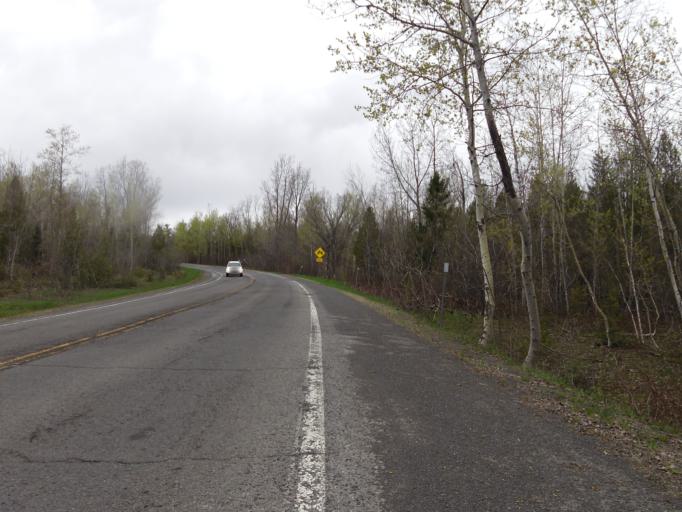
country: CA
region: Quebec
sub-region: Laurentides
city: Lachute
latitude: 45.5766
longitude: -74.3745
